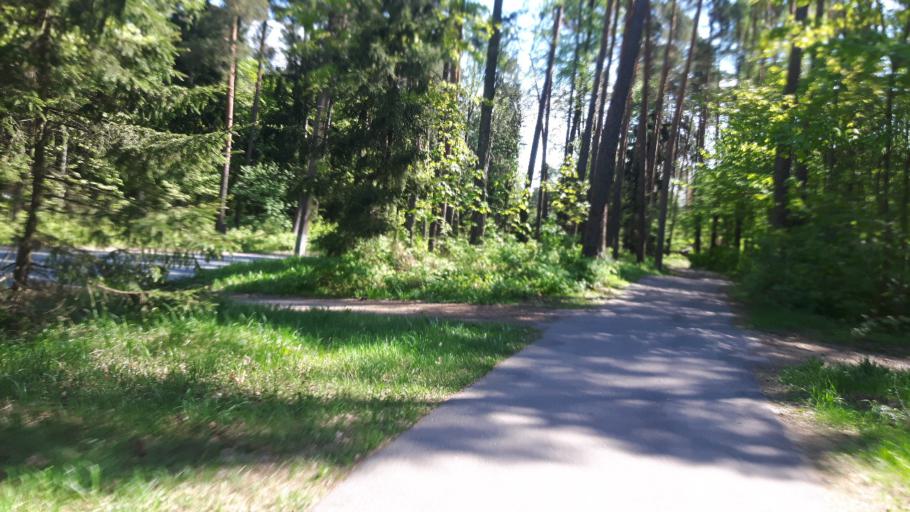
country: RU
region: St.-Petersburg
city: Komarovo
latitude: 60.1664
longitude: 29.8336
